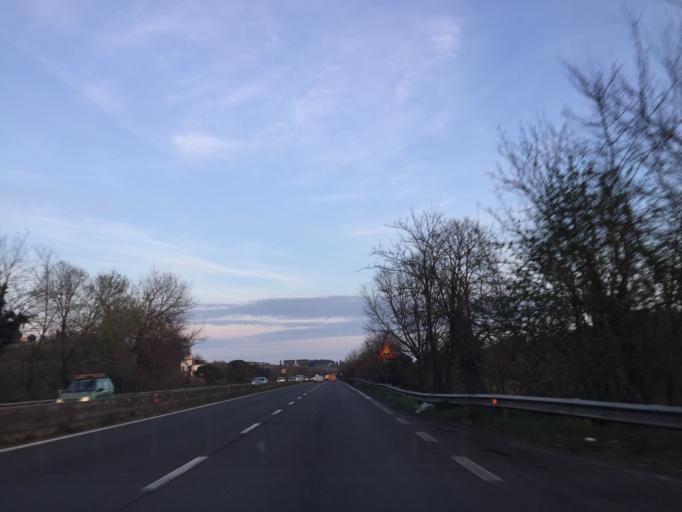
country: IT
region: Latium
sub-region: Citta metropolitana di Roma Capitale
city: Monte Caminetto
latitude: 41.9981
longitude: 12.4560
